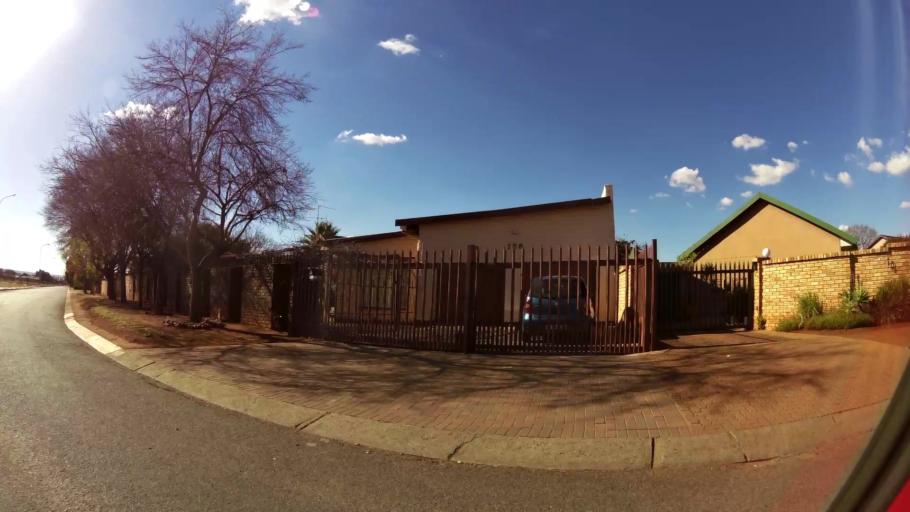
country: ZA
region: Gauteng
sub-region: West Rand District Municipality
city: Carletonville
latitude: -26.3637
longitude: 27.3763
